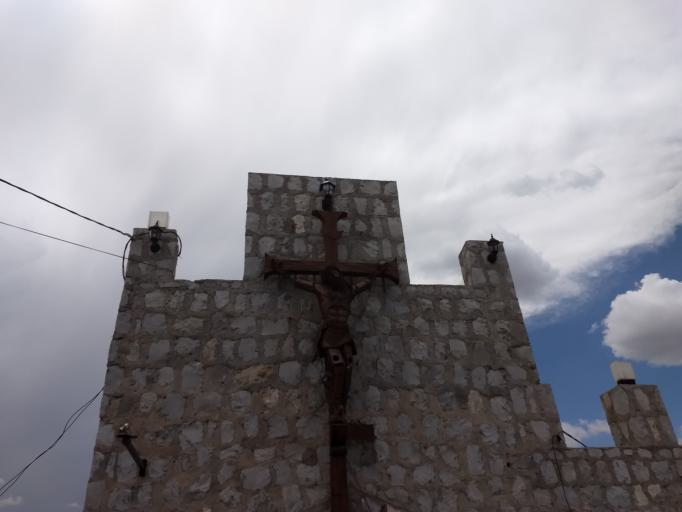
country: MX
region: Durango
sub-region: Lerdo
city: El Huarache (El Guarache)
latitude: 25.5258
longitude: -103.4564
